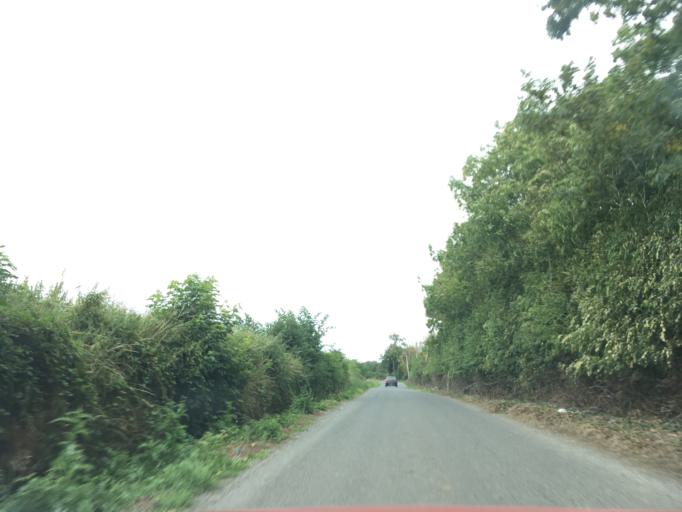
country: IE
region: Munster
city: Cahir
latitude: 52.4616
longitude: -8.0066
